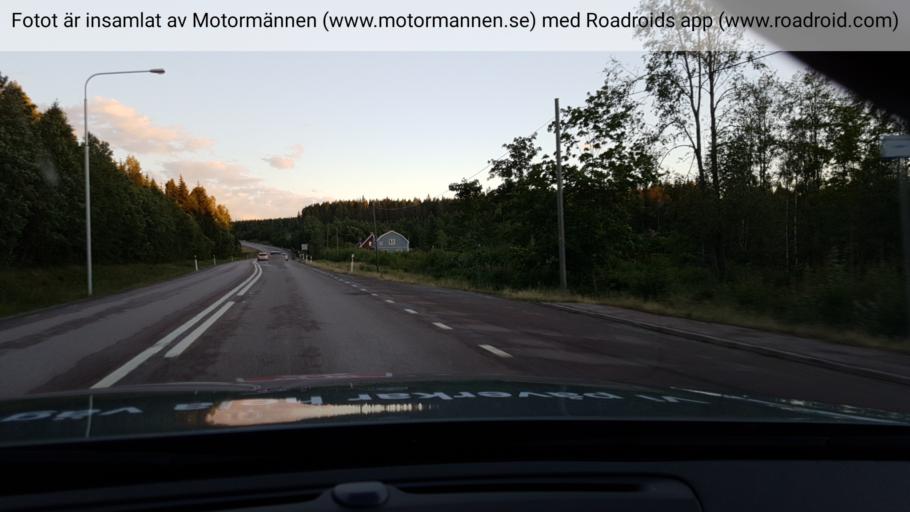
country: SE
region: Vaestmanland
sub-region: Fagersta Kommun
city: Fagersta
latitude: 59.9595
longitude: 15.7606
